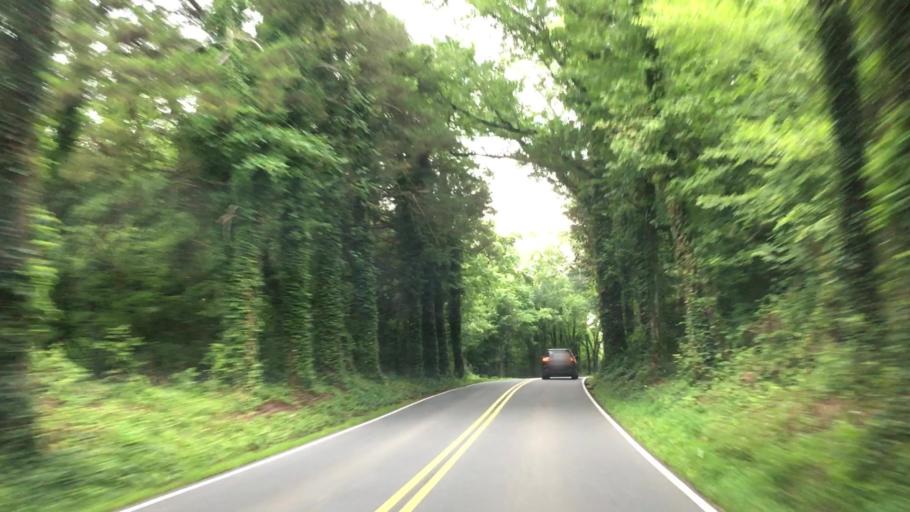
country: US
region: Virginia
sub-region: City of Fredericksburg
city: Fredericksburg
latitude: 38.3123
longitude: -77.4611
